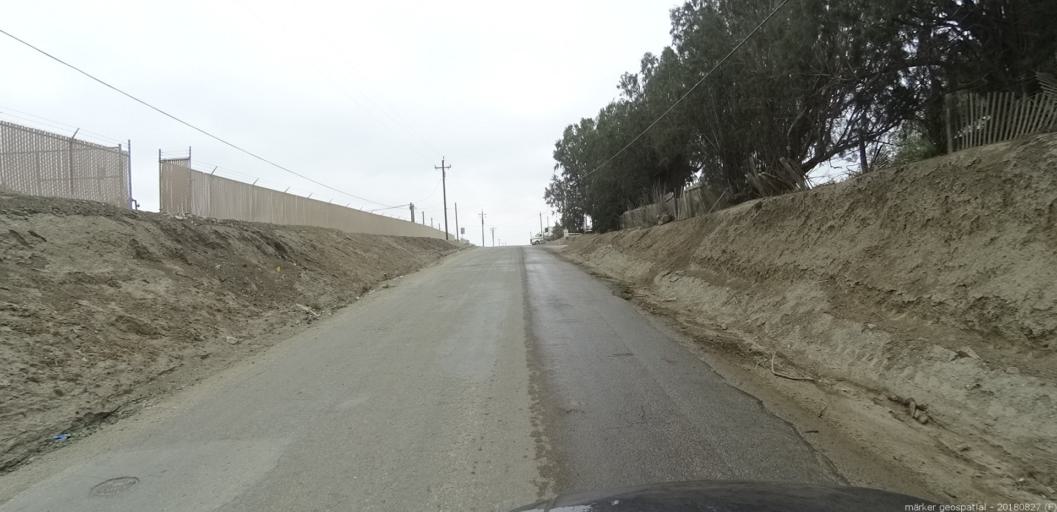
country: US
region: California
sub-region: Monterey County
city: King City
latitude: 36.2075
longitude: -121.1146
